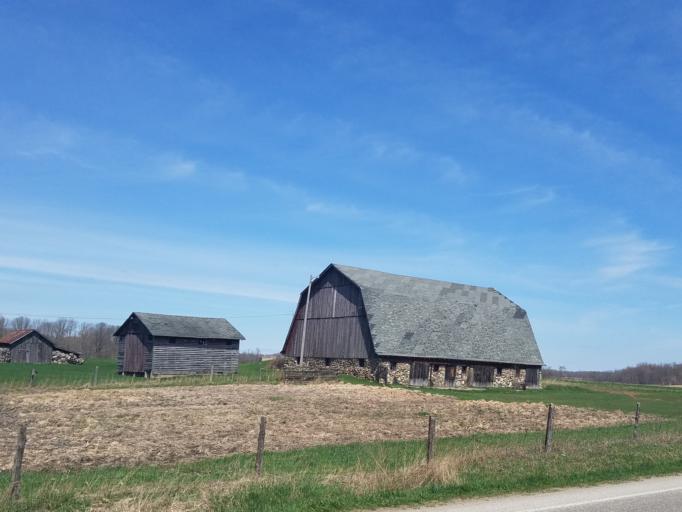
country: US
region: Michigan
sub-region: Midland County
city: Coleman
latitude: 43.8730
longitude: -84.6437
